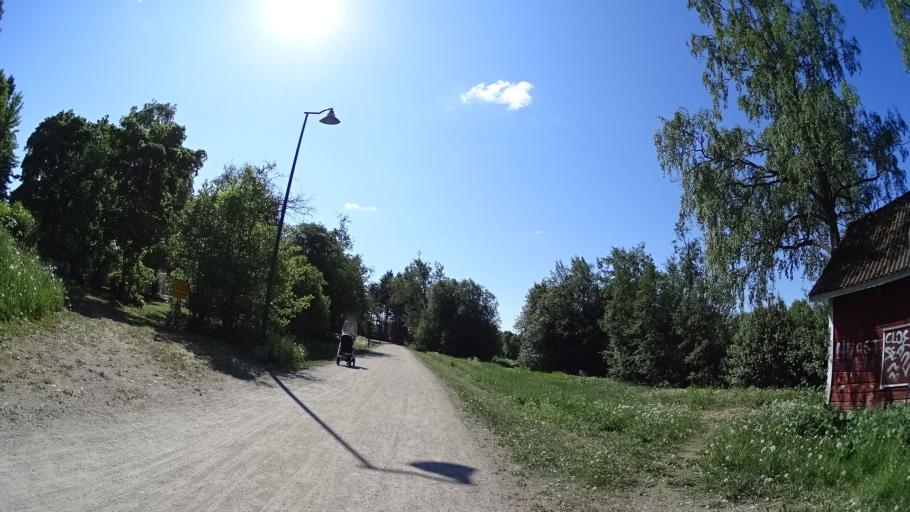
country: FI
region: Uusimaa
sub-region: Helsinki
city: Vantaa
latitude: 60.2721
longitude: 24.9571
